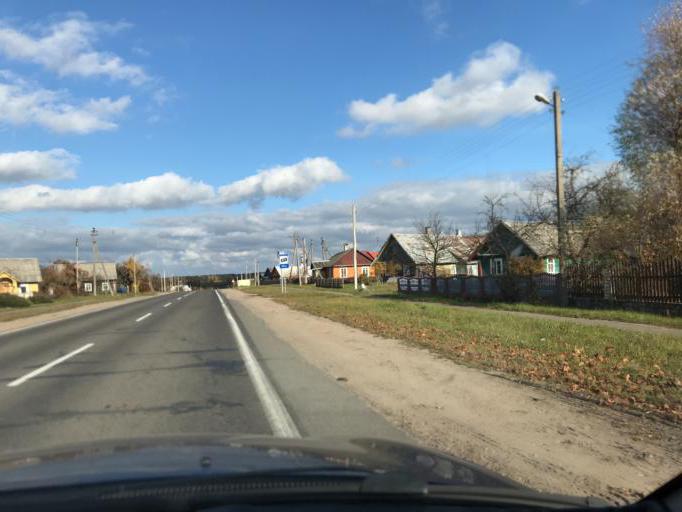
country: LT
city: Salcininkai
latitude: 54.2565
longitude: 25.3570
